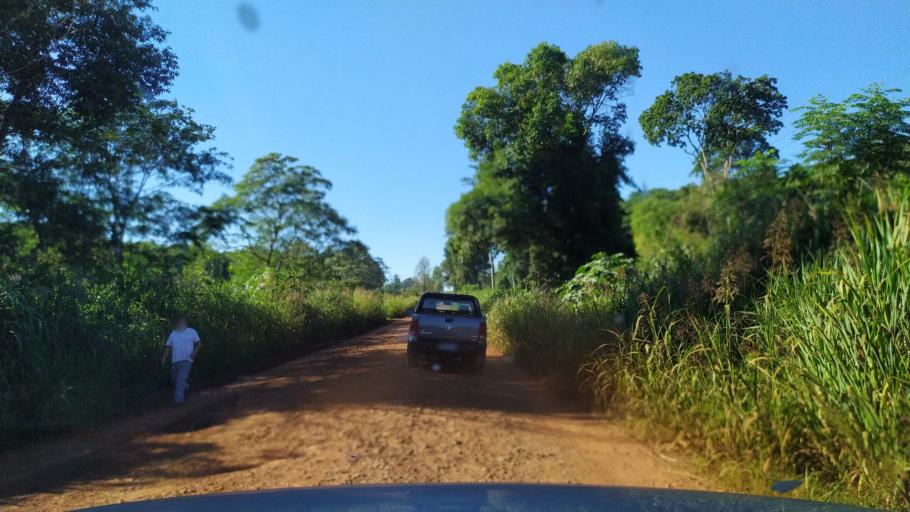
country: AR
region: Misiones
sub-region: Departamento de Montecarlo
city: Montecarlo
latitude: -26.6143
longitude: -54.6979
